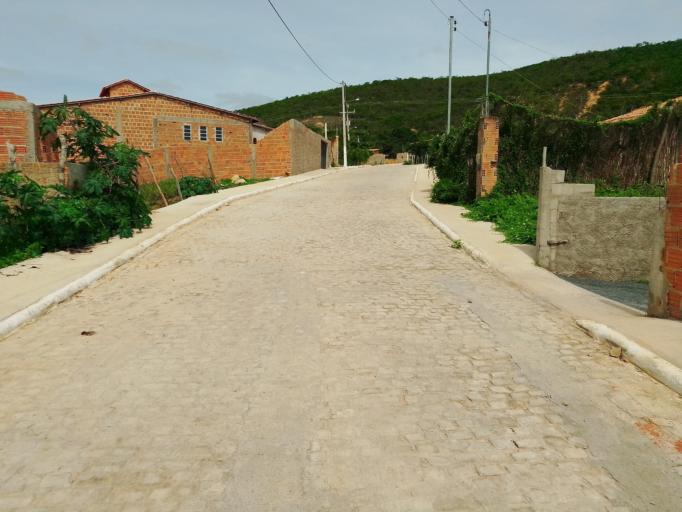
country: BR
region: Bahia
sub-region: Seabra
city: Seabra
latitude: -12.5127
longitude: -41.5793
